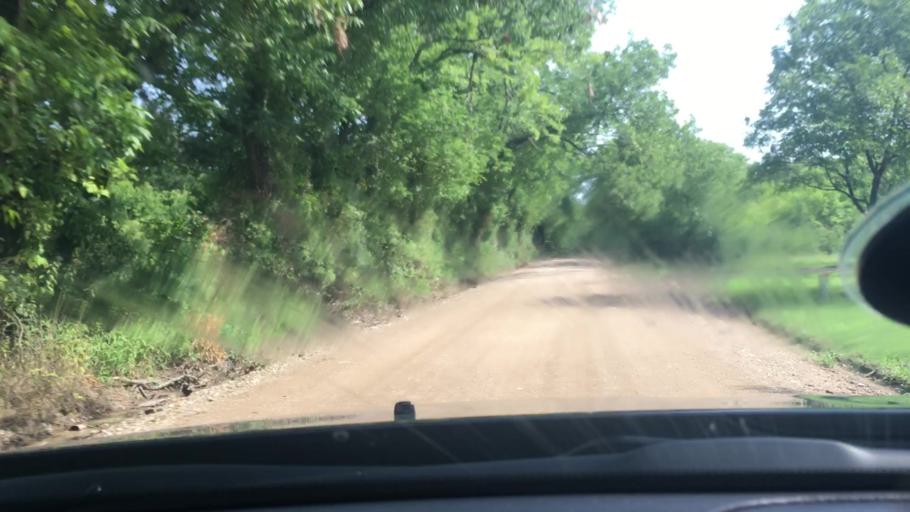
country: US
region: Oklahoma
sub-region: Atoka County
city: Atoka
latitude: 34.4539
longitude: -96.0658
